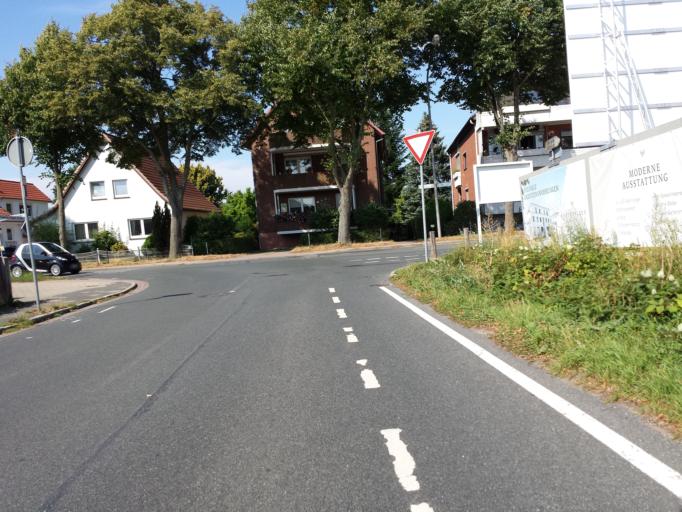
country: DE
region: Bremen
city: Bremen
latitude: 53.0503
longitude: 8.8529
